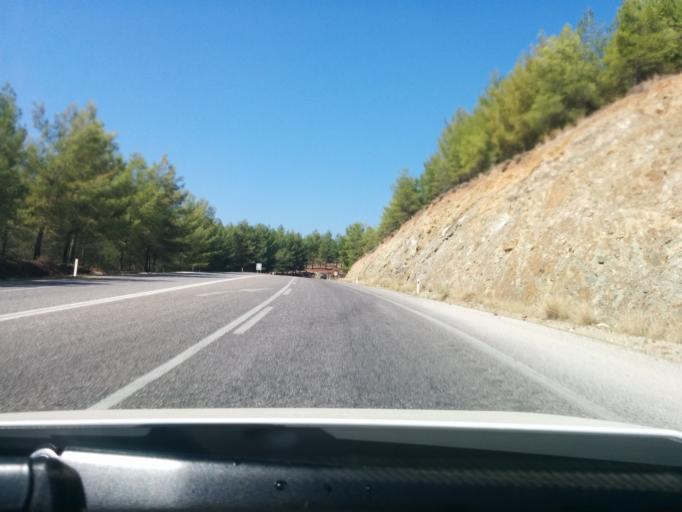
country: TR
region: Mugla
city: Kemer
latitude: 36.6179
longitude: 29.3557
